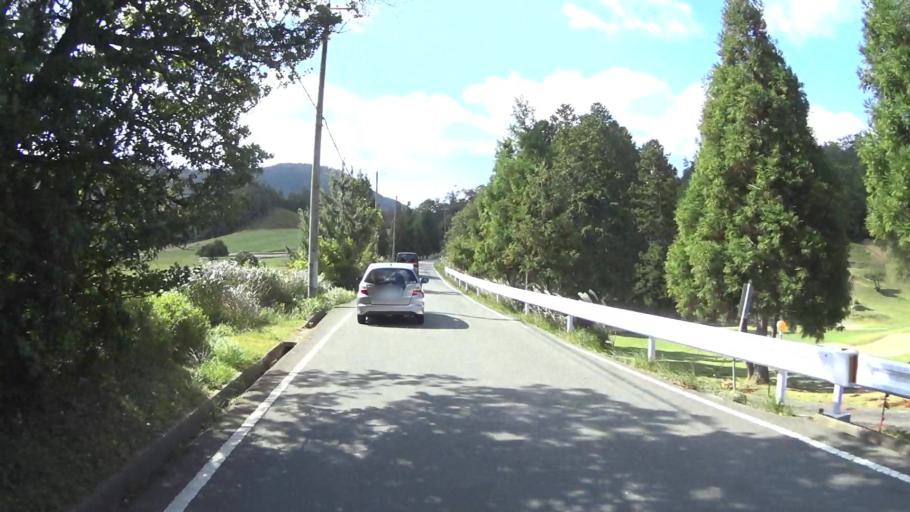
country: JP
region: Kyoto
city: Kameoka
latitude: 35.1659
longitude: 135.4537
